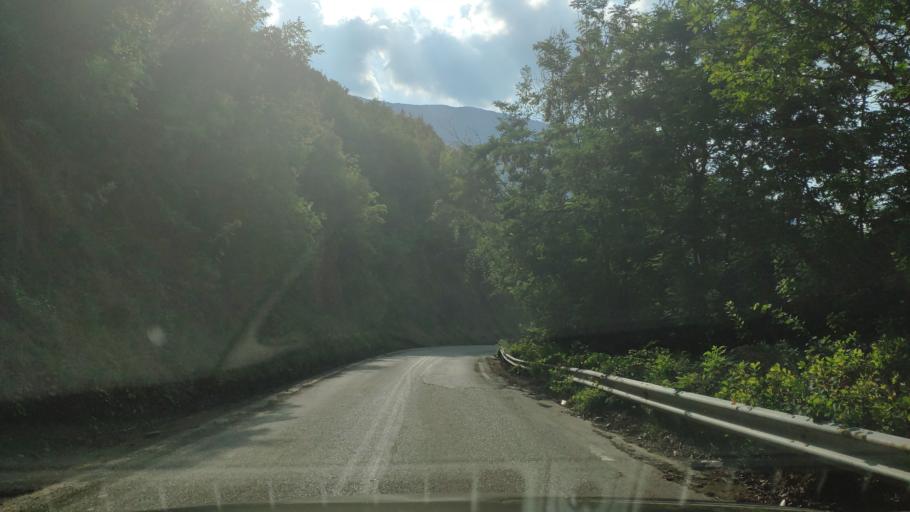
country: GR
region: Epirus
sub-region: Nomos Artas
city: Agios Dimitrios
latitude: 39.4574
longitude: 21.0434
